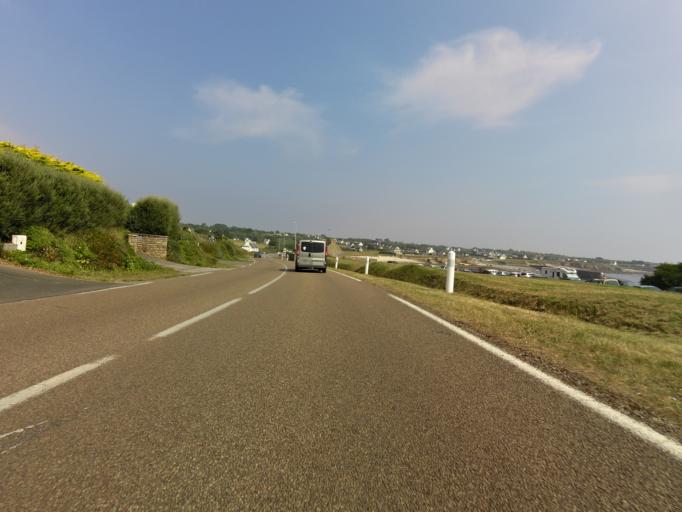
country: FR
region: Brittany
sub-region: Departement du Finistere
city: Plogoff
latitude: 48.0294
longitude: -4.6367
